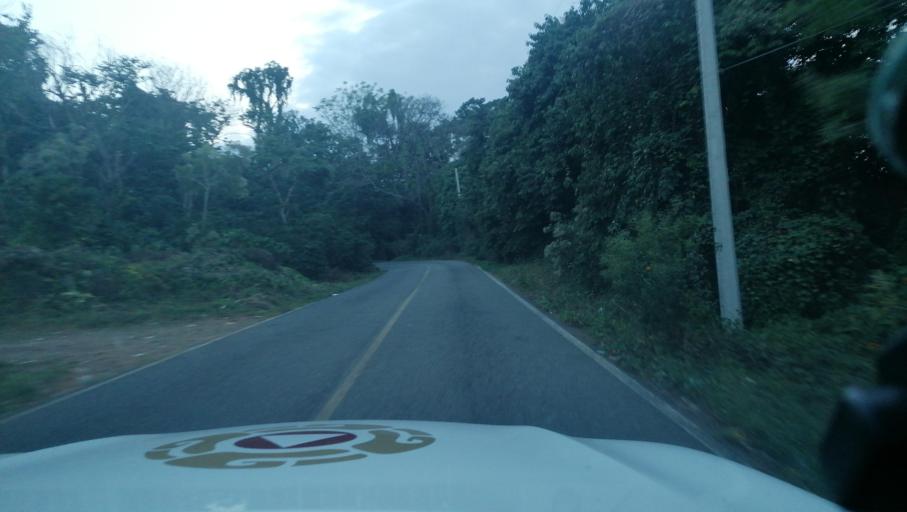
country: MX
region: Chiapas
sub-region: Cacahoatan
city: Benito Juarez
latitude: 15.0354
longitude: -92.2420
